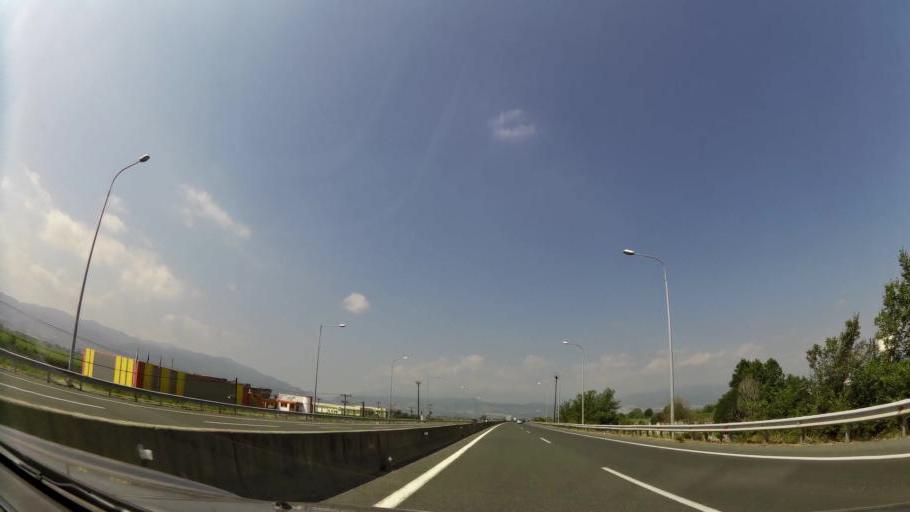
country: GR
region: Central Macedonia
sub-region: Nomos Imathias
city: Kouloura
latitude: 40.5392
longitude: 22.3122
